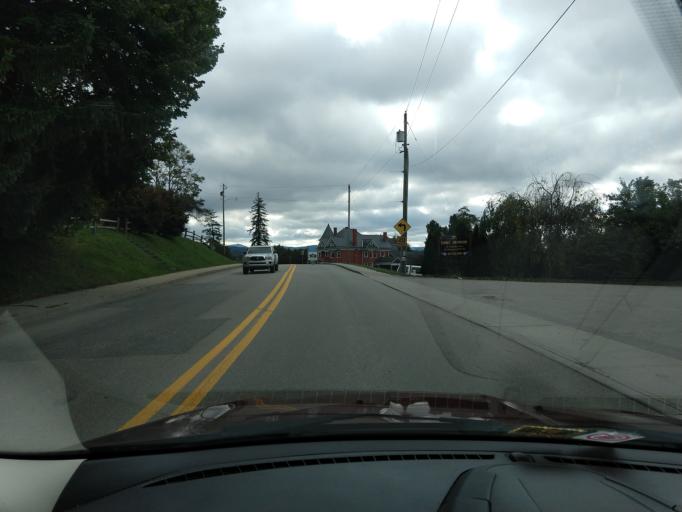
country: US
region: West Virginia
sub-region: Randolph County
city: Elkins
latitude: 38.9284
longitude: -79.8588
